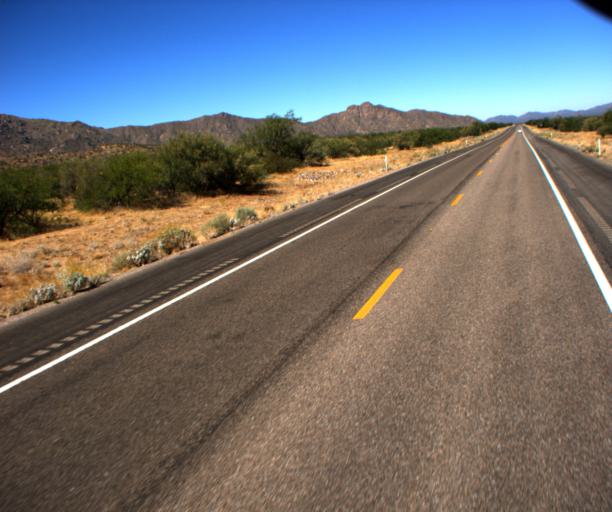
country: US
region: Arizona
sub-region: Pima County
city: Sells
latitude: 32.0190
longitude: -111.6178
